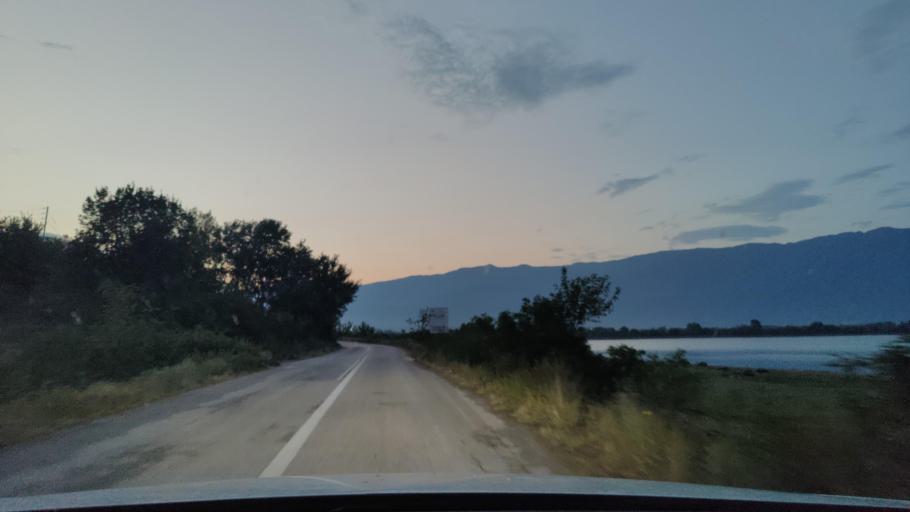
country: GR
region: Central Macedonia
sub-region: Nomos Serron
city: Chrysochorafa
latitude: 41.1966
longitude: 23.0920
